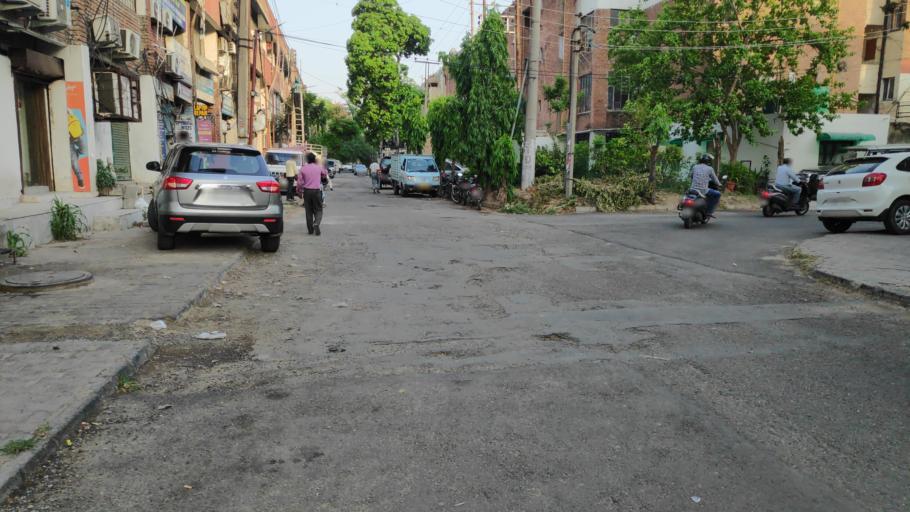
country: IN
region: Chandigarh
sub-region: Chandigarh
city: Chandigarh
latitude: 30.7146
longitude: 76.7508
